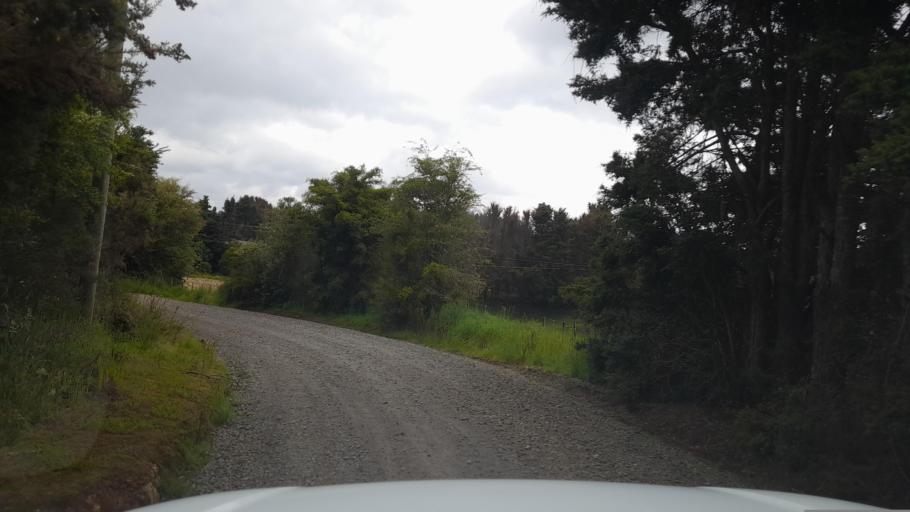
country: NZ
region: Northland
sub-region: Far North District
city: Waimate North
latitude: -35.3979
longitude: 173.7845
